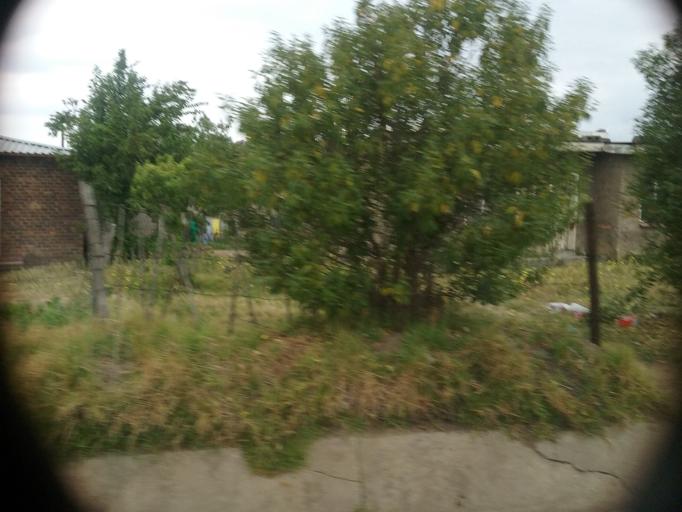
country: LS
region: Maseru
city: Maseru
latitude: -29.3203
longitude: 27.5100
